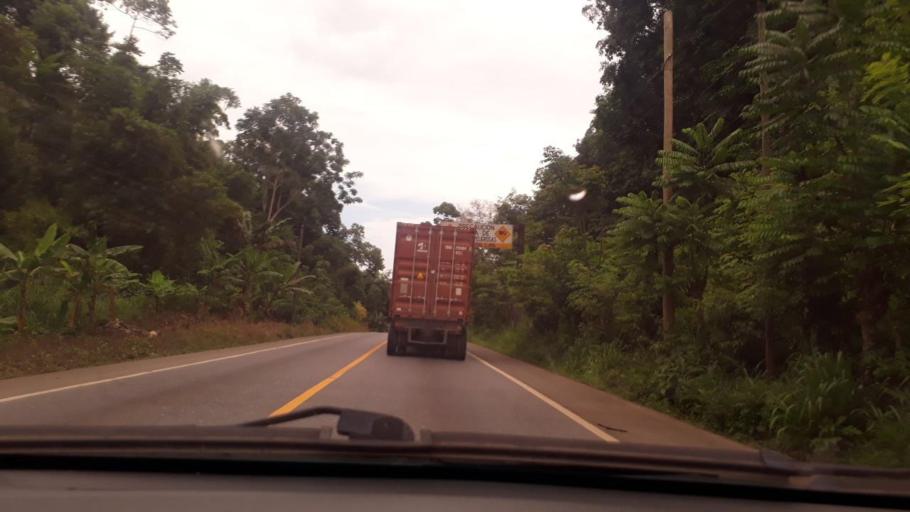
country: GT
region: Izabal
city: Morales
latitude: 15.5569
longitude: -88.6734
